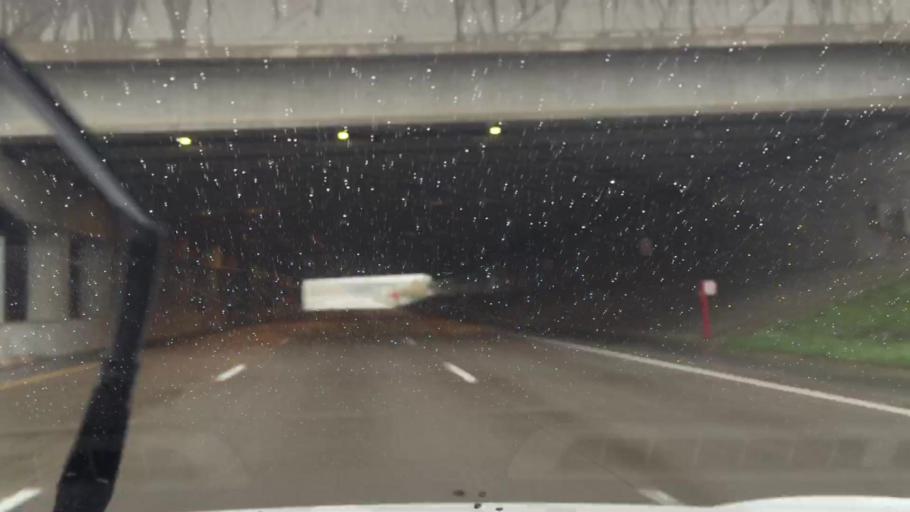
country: CA
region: Ontario
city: Windsor
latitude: 42.2409
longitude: -83.0110
